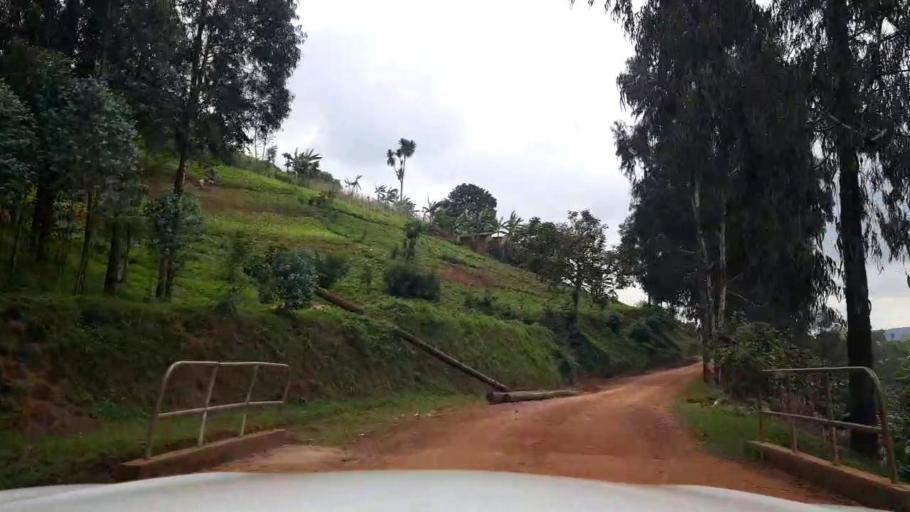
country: UG
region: Western Region
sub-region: Kabale District
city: Kabale
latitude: -1.4265
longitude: 29.8685
